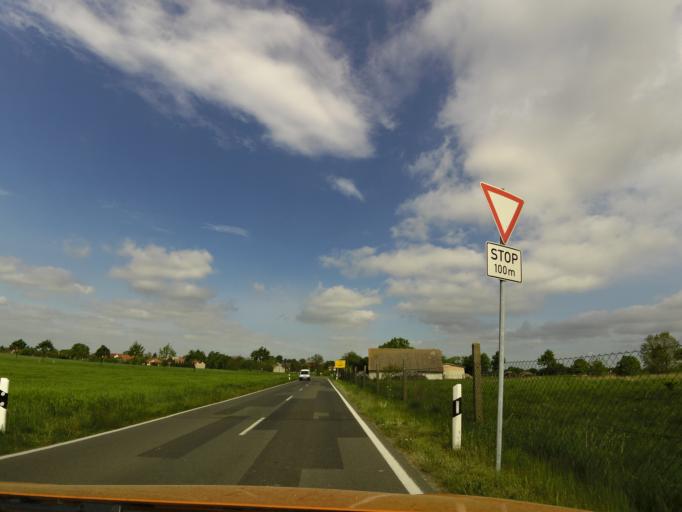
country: DE
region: Brandenburg
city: Belzig
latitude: 52.1001
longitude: 12.5621
